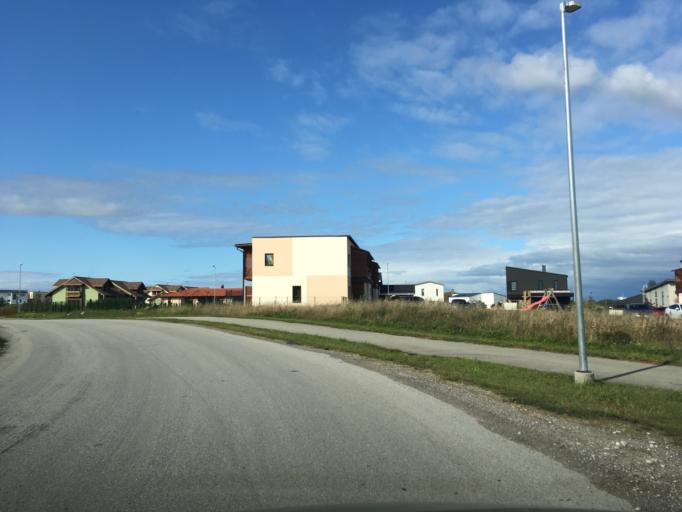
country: EE
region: Harju
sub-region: Saue vald
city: Laagri
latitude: 59.3452
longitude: 24.6462
